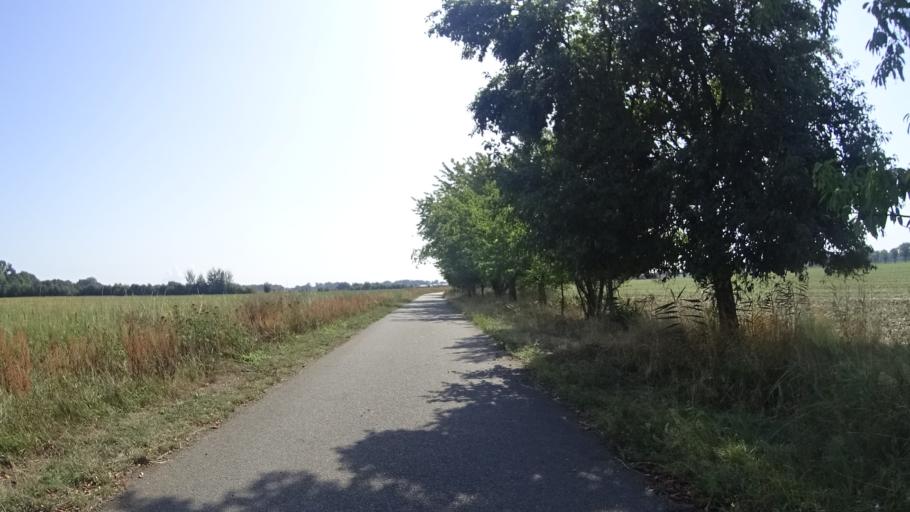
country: DE
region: Brandenburg
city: Werben
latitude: 51.8218
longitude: 14.1642
